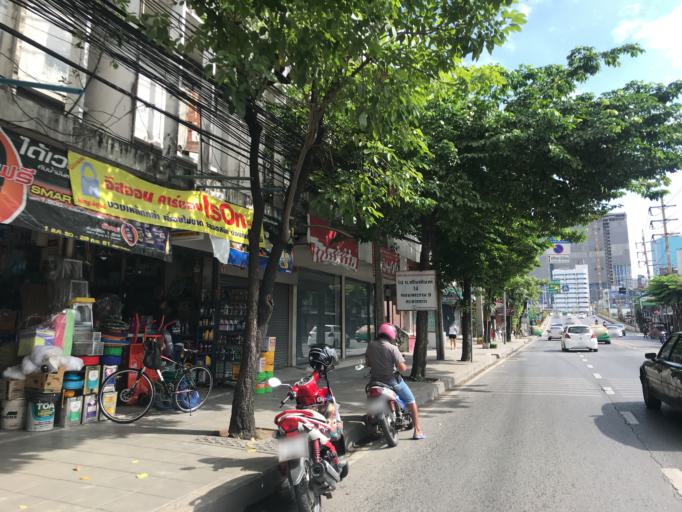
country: TH
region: Bangkok
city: Watthana
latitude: 13.7359
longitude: 100.5979
